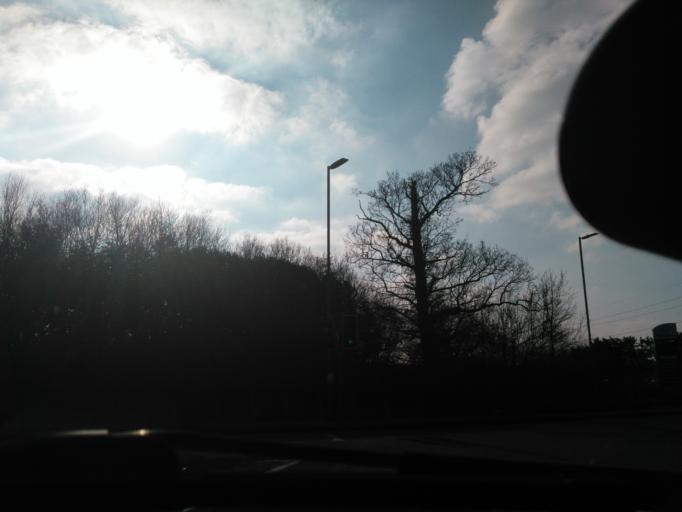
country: GB
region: England
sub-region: Wiltshire
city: Chippenham
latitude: 51.4781
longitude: -2.1282
